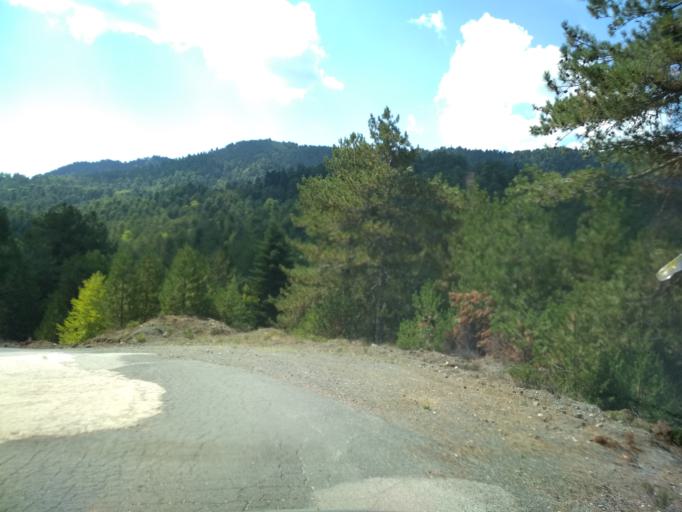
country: GR
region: Central Greece
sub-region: Nomos Evvoias
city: Roviai
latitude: 38.8676
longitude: 23.2905
